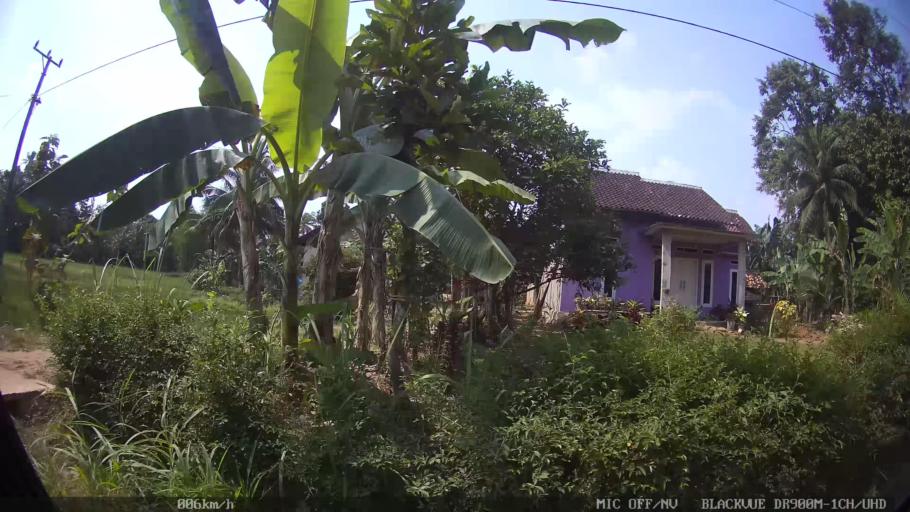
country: ID
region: Lampung
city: Natar
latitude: -5.2938
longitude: 105.2401
